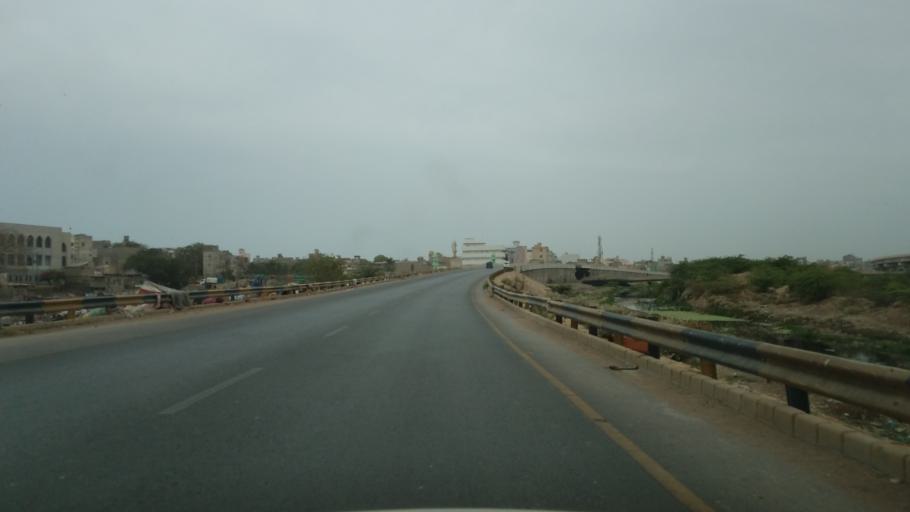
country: PK
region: Sindh
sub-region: Karachi District
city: Karachi
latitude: 24.8789
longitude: 67.0155
